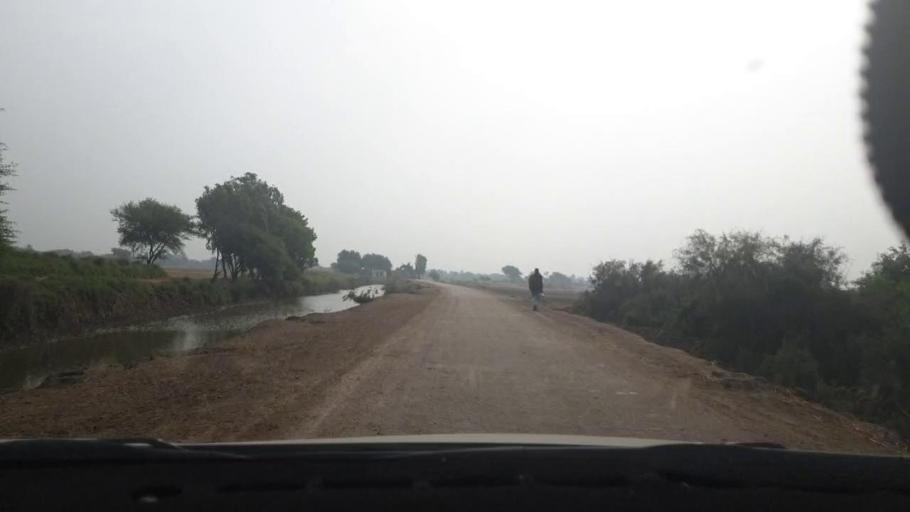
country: PK
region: Sindh
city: Tando Muhammad Khan
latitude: 25.0555
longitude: 68.5476
